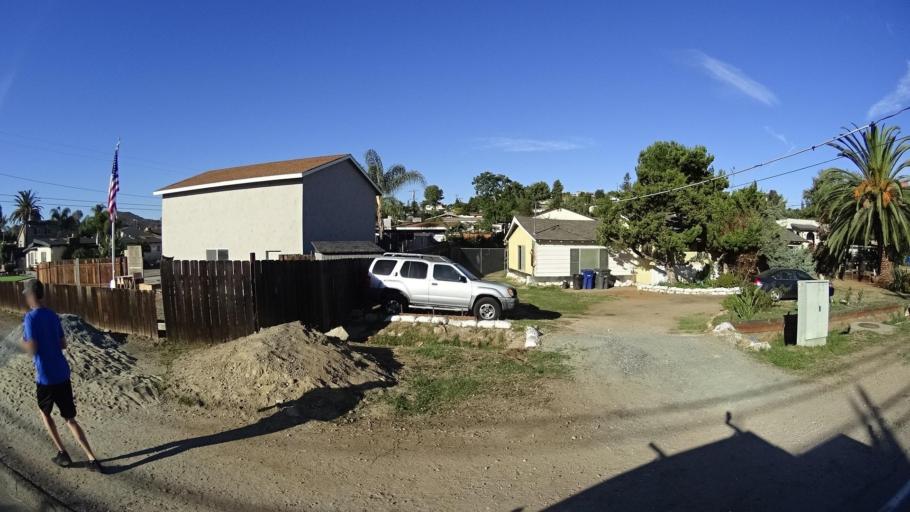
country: US
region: California
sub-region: San Diego County
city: Lakeside
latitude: 32.8454
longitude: -116.9049
